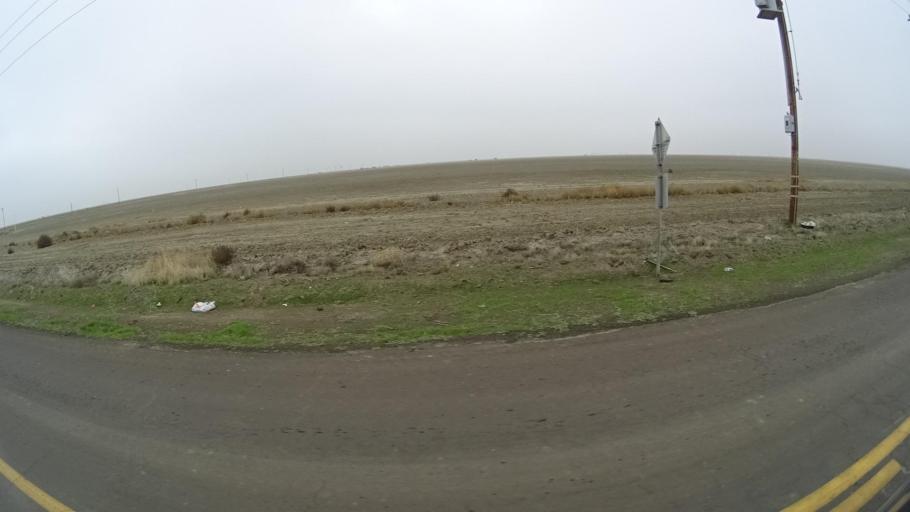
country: US
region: California
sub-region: Tulare County
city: Alpaugh
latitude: 35.7028
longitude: -119.5064
